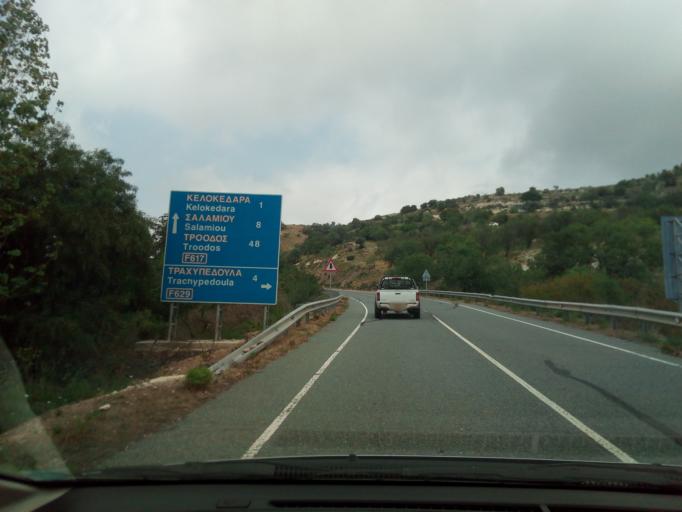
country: CY
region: Limassol
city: Pissouri
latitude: 34.8012
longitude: 32.6493
